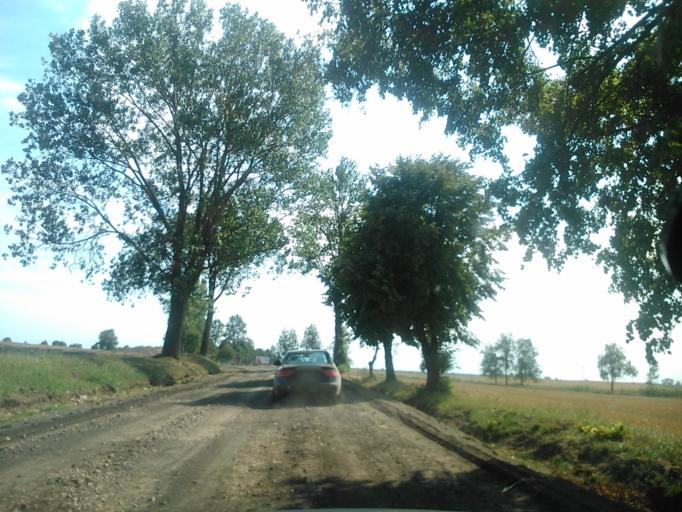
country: PL
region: Warmian-Masurian Voivodeship
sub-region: Powiat dzialdowski
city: Ilowo -Osada
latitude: 53.2072
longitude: 20.2348
